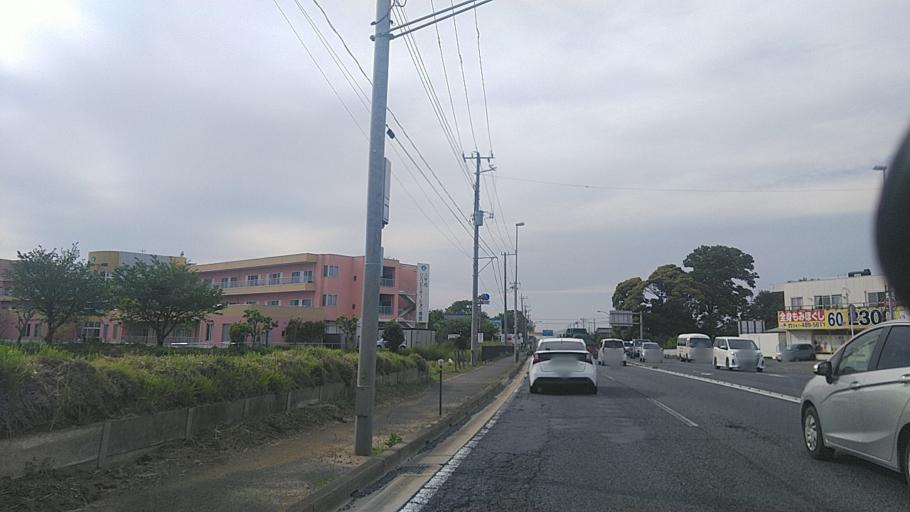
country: JP
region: Chiba
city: Shiroi
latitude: 35.7462
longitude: 140.1202
